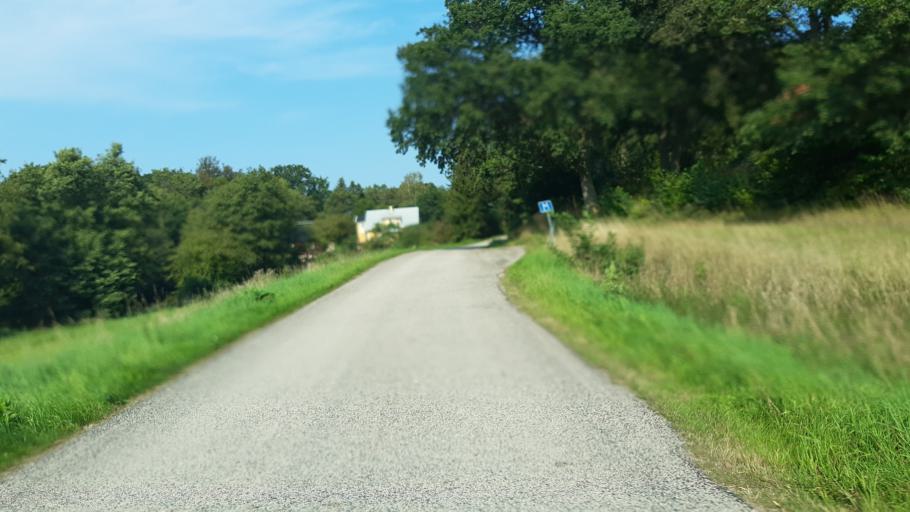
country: SE
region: Blekinge
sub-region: Ronneby Kommun
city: Brakne-Hoby
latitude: 56.1953
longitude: 15.1012
